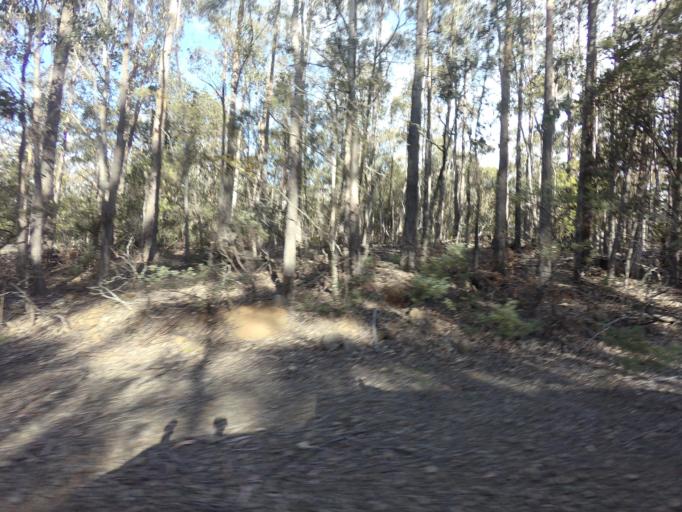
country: AU
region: Tasmania
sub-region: Break O'Day
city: St Helens
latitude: -41.8439
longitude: 148.0619
